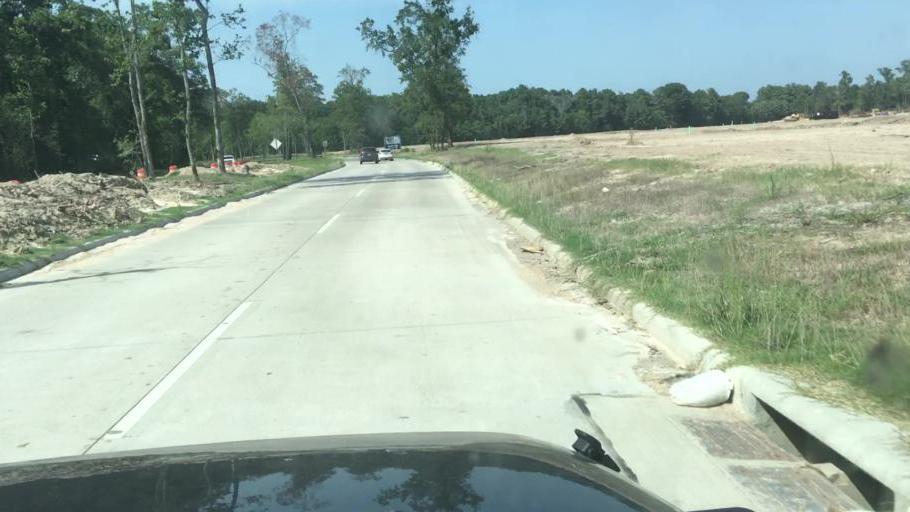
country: US
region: Texas
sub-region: Harris County
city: Atascocita
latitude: 29.9510
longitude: -95.2106
